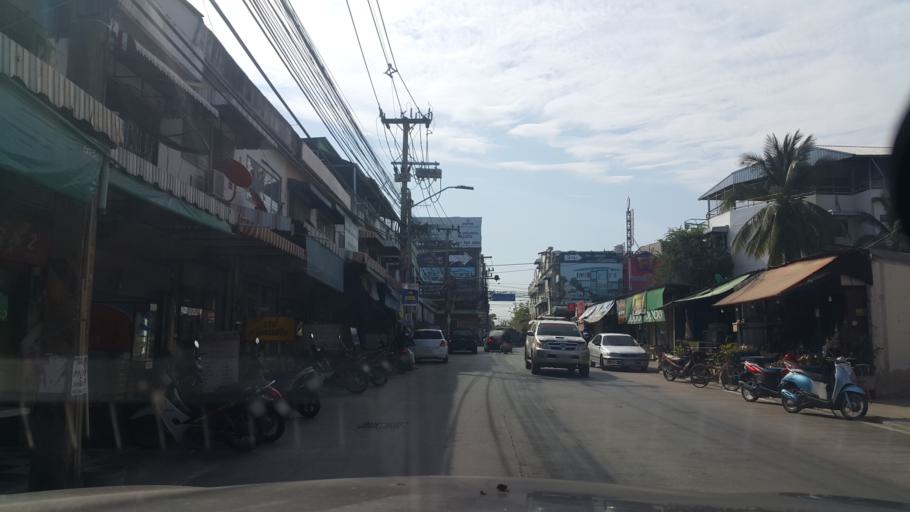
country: TH
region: Nakhon Ratchasima
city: Nakhon Ratchasima
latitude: 14.9496
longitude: 102.0447
